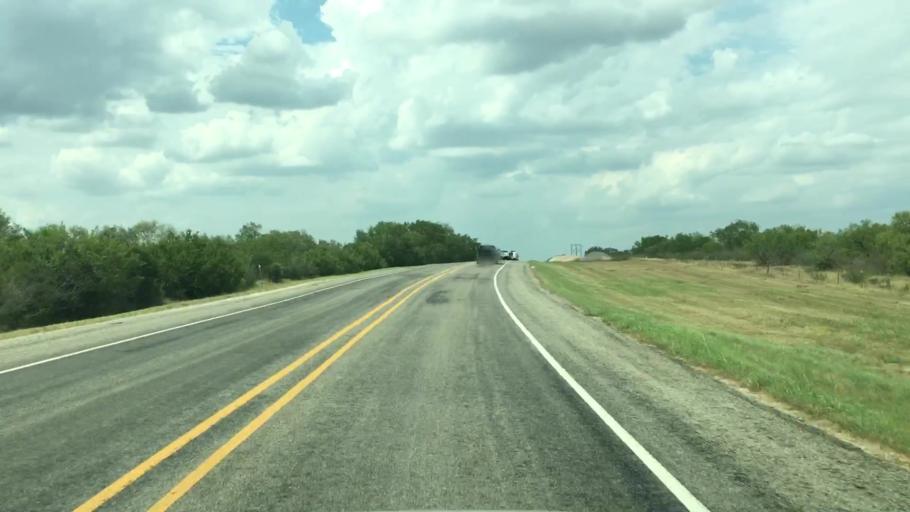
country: US
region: Texas
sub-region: Live Oak County
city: Three Rivers
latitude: 28.6440
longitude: -98.2843
